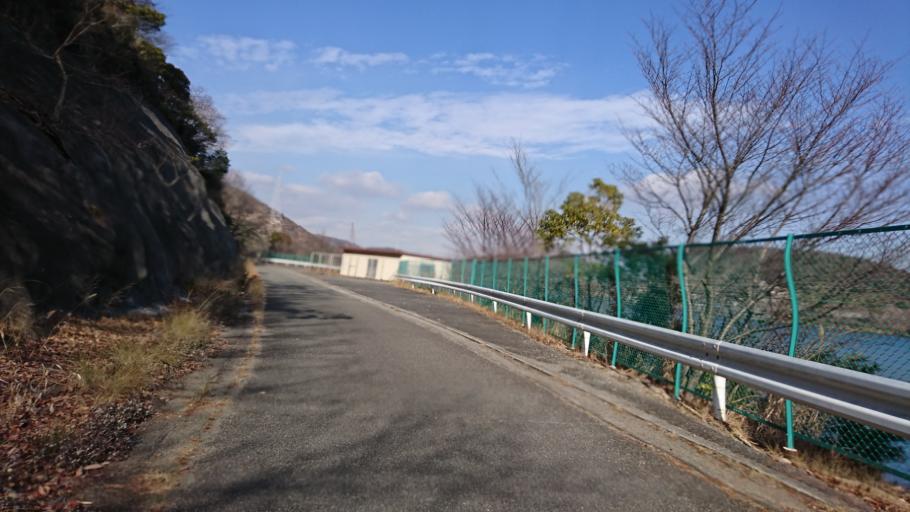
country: JP
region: Hyogo
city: Kakogawacho-honmachi
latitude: 34.8200
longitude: 134.8730
